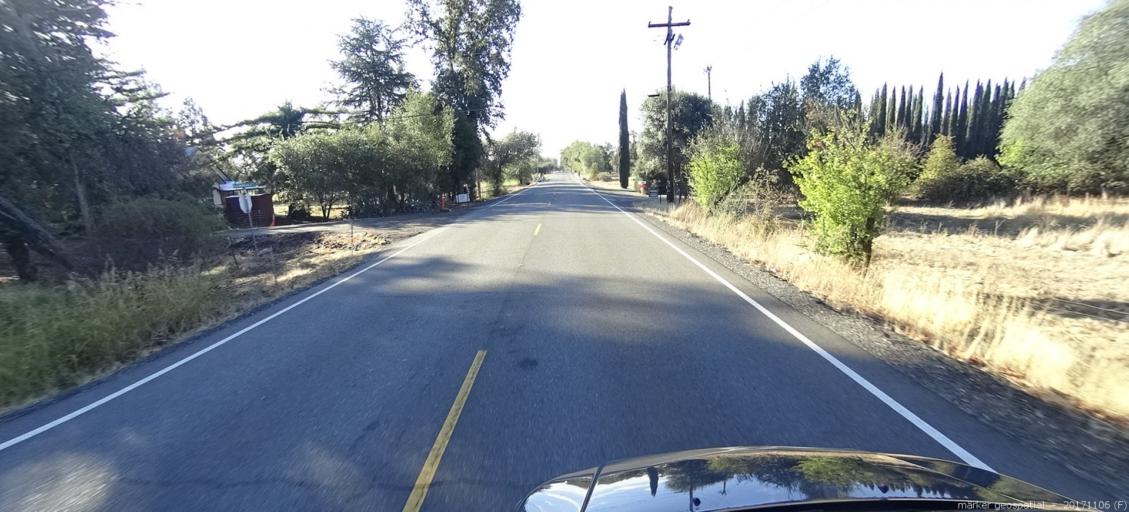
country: US
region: California
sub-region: Shasta County
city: Bella Vista
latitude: 40.6063
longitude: -122.2346
